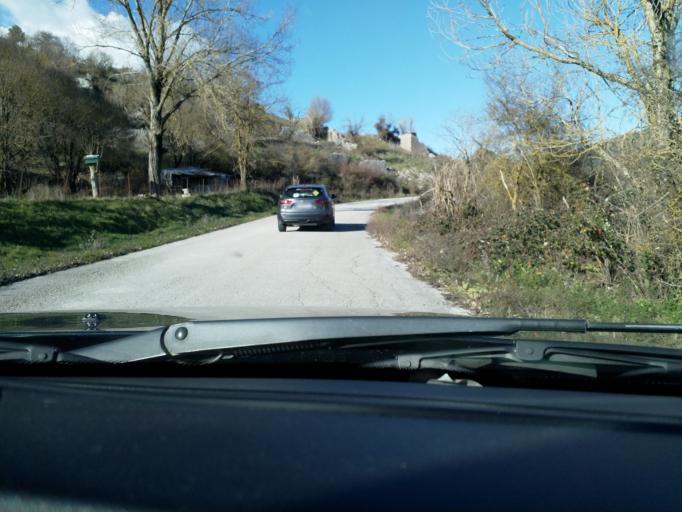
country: GR
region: Epirus
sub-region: Nomos Ioanninon
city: Kalpaki
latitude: 39.8808
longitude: 20.6773
